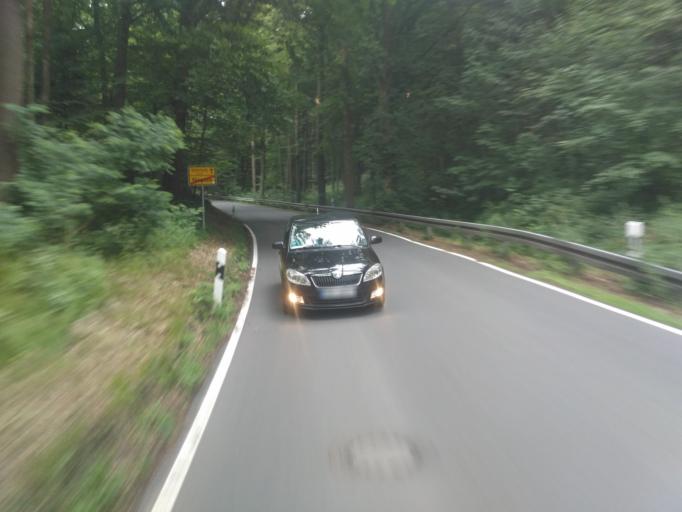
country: DE
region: Saxony
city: Kurort Gohrisch
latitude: 50.9186
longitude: 14.0926
